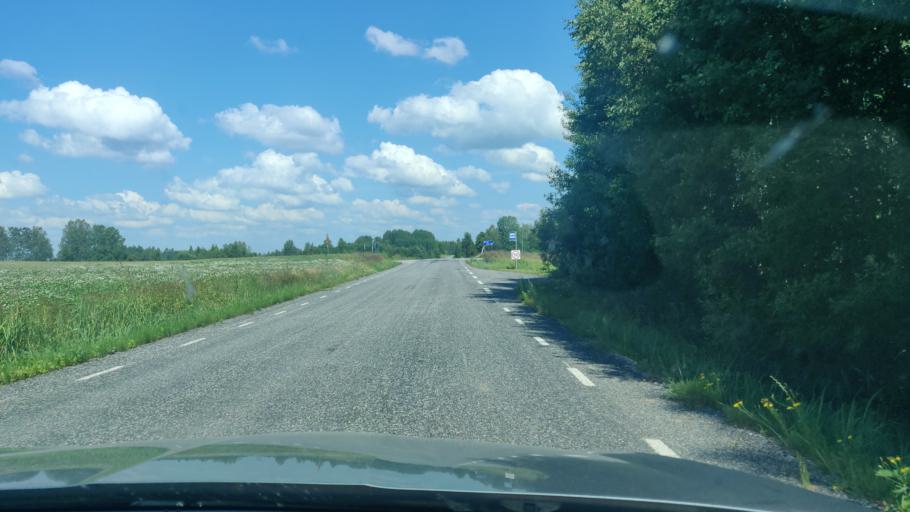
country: EE
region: Tartu
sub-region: Elva linn
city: Elva
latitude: 58.1427
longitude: 26.4766
